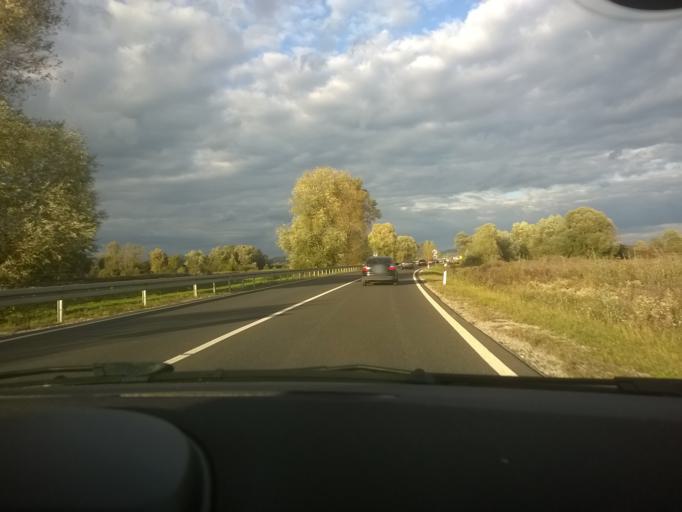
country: HR
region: Zagrebacka
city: Jakovlje
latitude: 45.9874
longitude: 15.8478
